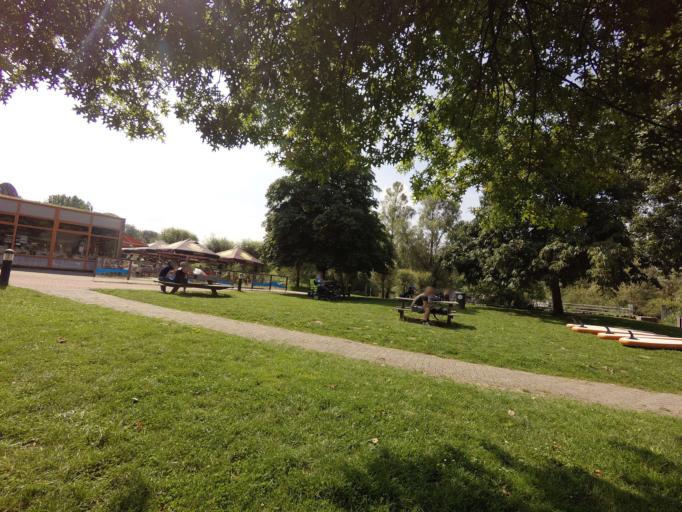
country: NL
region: South Holland
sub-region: Gemeente Sliedrecht
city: Sliedrecht
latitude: 51.8074
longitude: 4.7638
